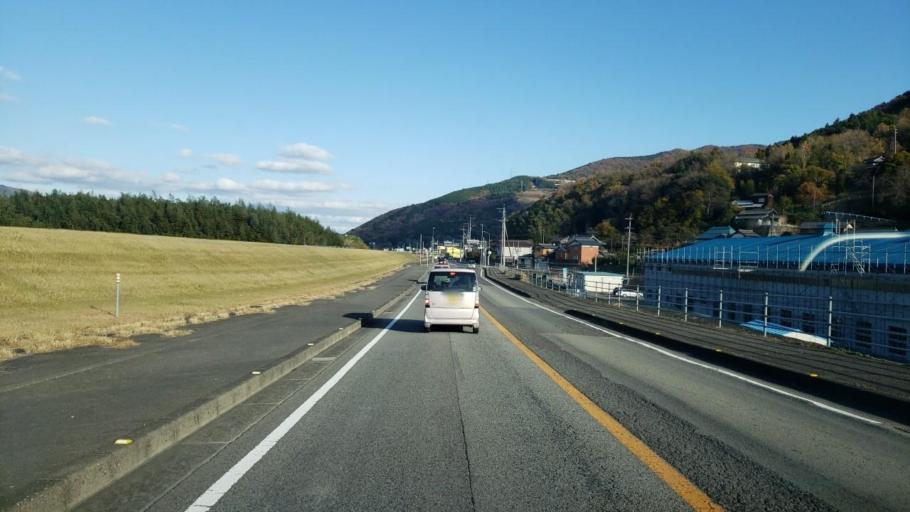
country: JP
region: Tokushima
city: Wakimachi
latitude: 34.0443
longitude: 134.0681
